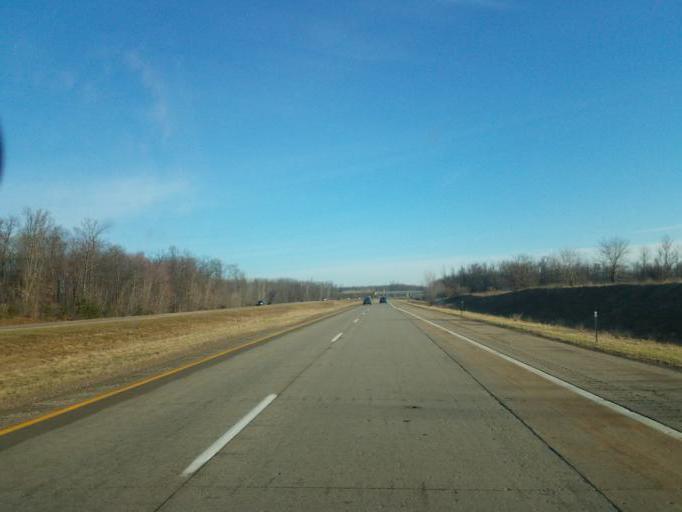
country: US
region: Michigan
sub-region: Clinton County
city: DeWitt
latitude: 42.8642
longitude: -84.5185
